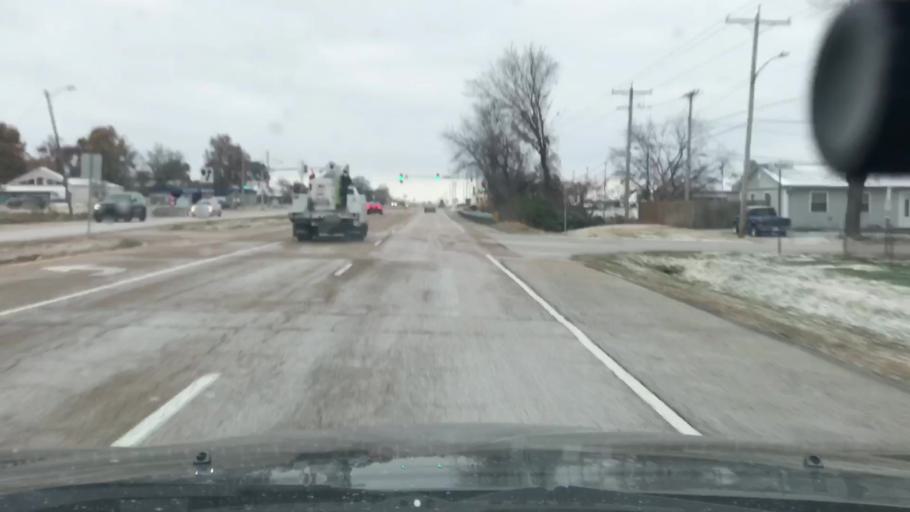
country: US
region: Illinois
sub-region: Madison County
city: Pontoon Beach
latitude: 38.7309
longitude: -90.0709
